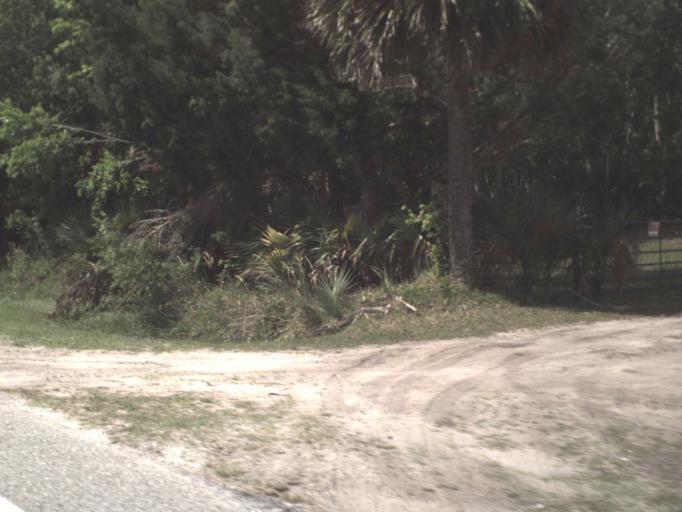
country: US
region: Florida
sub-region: Flagler County
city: Bunnell
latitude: 29.4866
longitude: -81.2667
